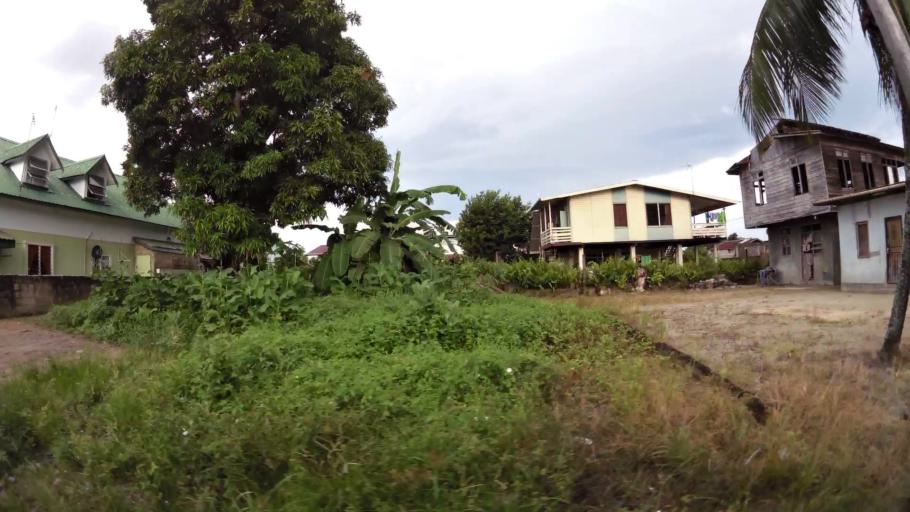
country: SR
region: Paramaribo
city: Paramaribo
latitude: 5.8363
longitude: -55.1794
